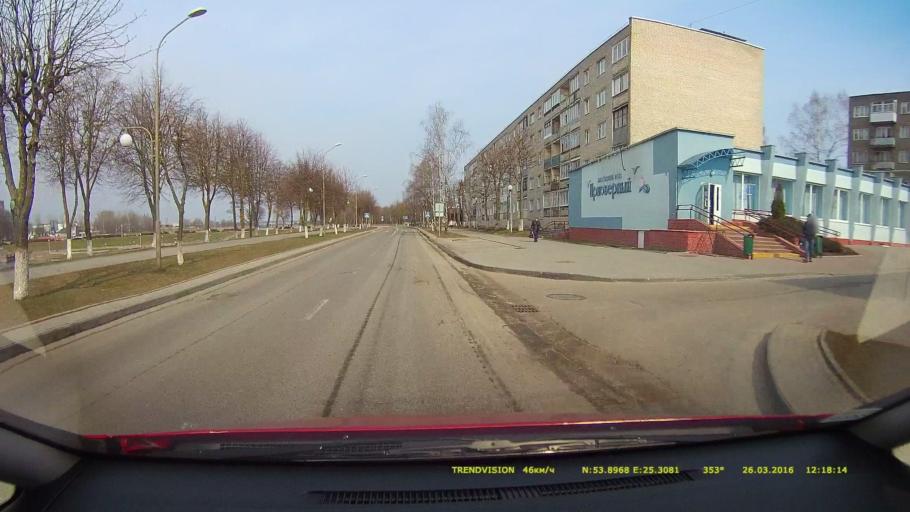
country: BY
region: Grodnenskaya
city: Lida
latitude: 53.8969
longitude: 25.3081
